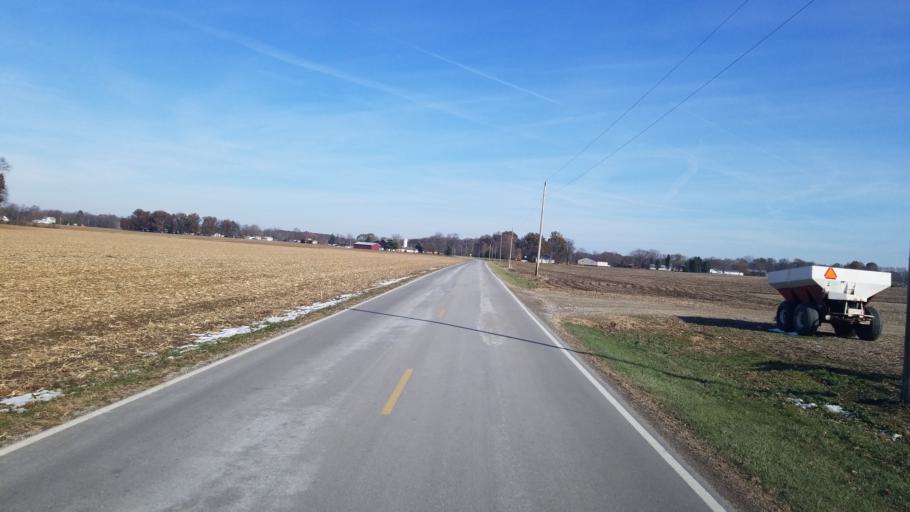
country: US
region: Ohio
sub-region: Huron County
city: Norwalk
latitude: 41.2098
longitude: -82.6463
